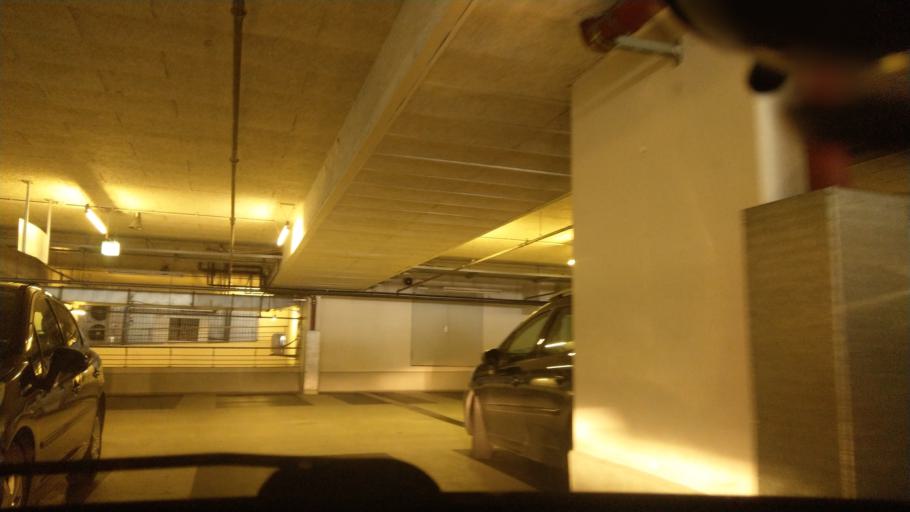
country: DE
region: Baden-Wuerttemberg
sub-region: Regierungsbezirk Stuttgart
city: Nurtingen
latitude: 48.6278
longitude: 9.3403
